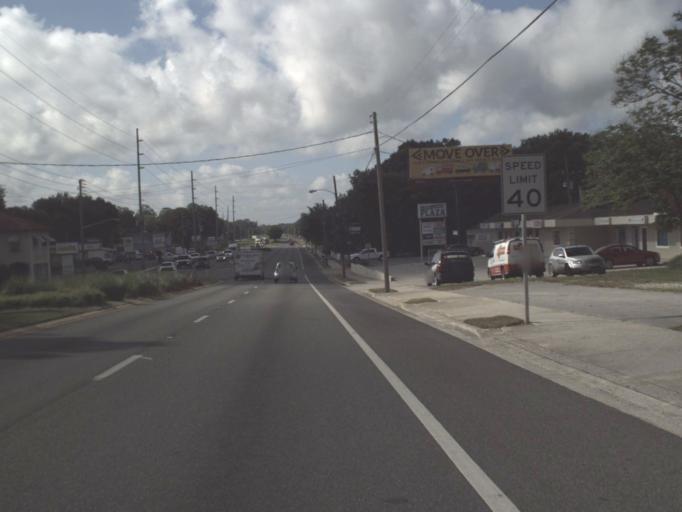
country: US
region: Florida
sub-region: Lake County
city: Lady Lake
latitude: 28.9154
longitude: -81.9215
